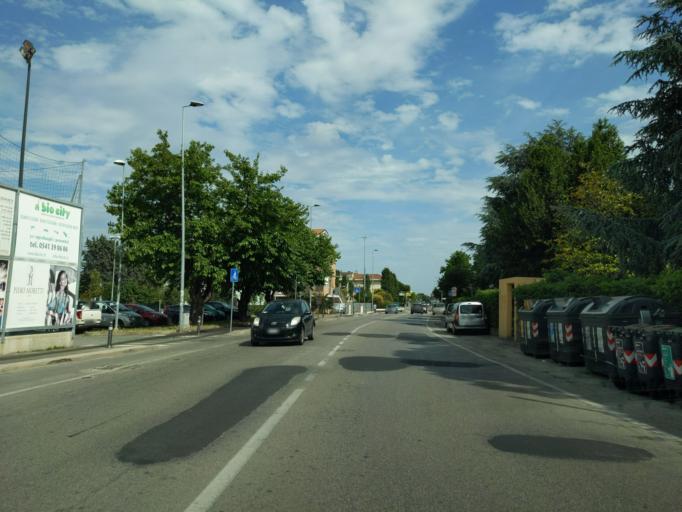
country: IT
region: Emilia-Romagna
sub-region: Provincia di Rimini
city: Rimini
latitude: 44.0459
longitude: 12.5835
